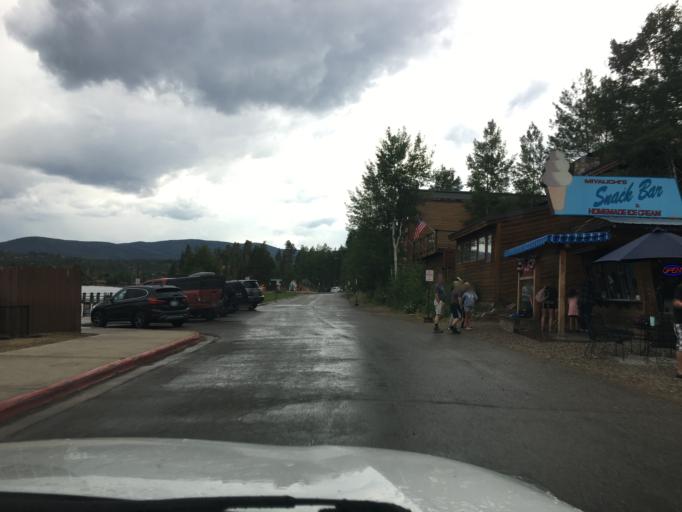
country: US
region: Colorado
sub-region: Grand County
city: Granby
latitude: 40.2506
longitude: -105.8184
